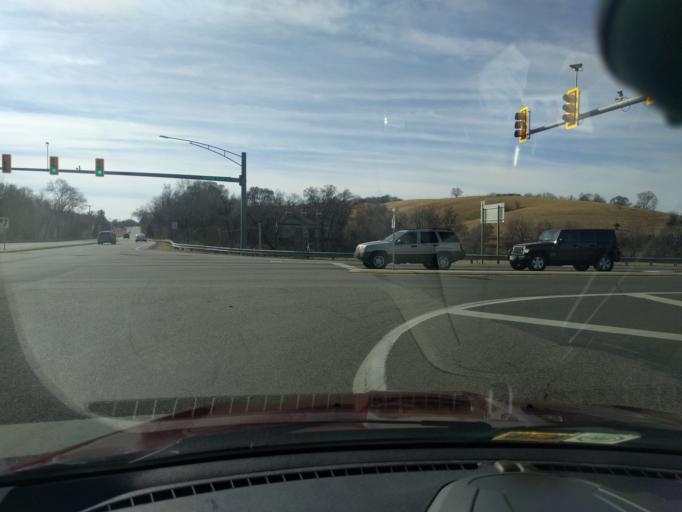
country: US
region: Virginia
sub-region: Augusta County
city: Verona
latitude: 38.1812
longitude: -79.0320
